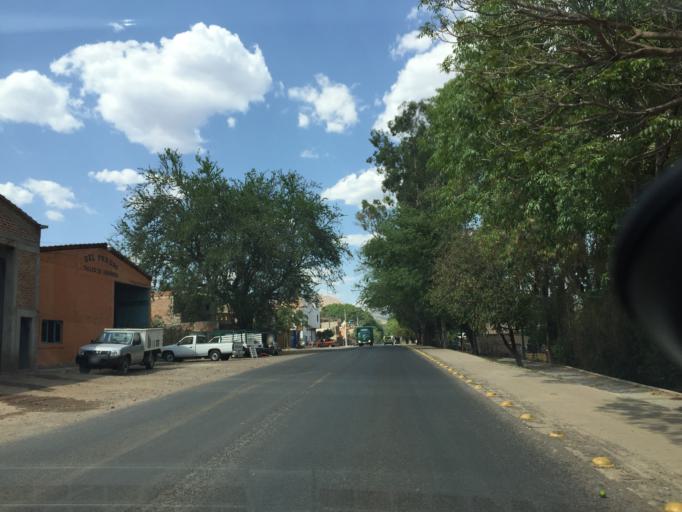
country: MX
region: Jalisco
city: Atotonilco el Alto
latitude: 20.5535
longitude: -102.4968
